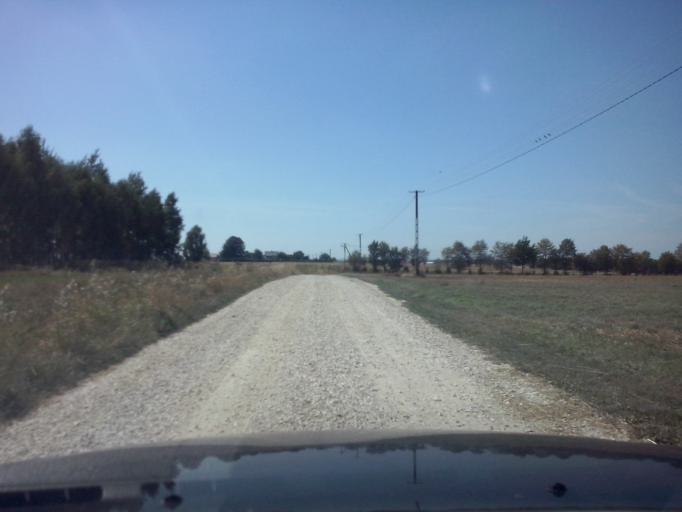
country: PL
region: Swietokrzyskie
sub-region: Powiat buski
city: Gnojno
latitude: 50.5983
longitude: 20.9007
